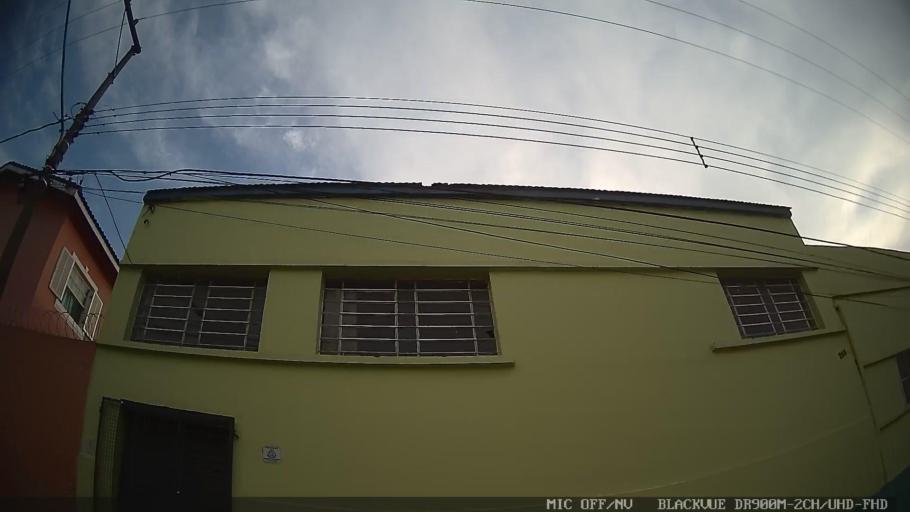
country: BR
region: Sao Paulo
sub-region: Braganca Paulista
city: Braganca Paulista
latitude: -22.9457
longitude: -46.5373
